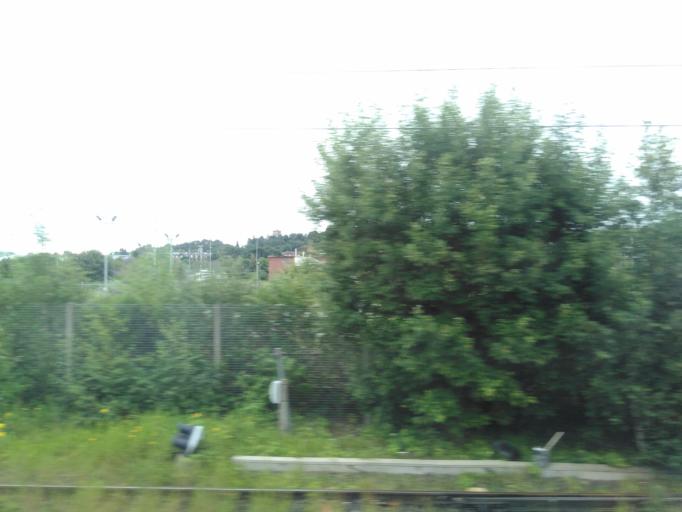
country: GB
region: Scotland
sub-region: Edinburgh
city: Colinton
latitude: 55.9287
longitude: -3.2395
